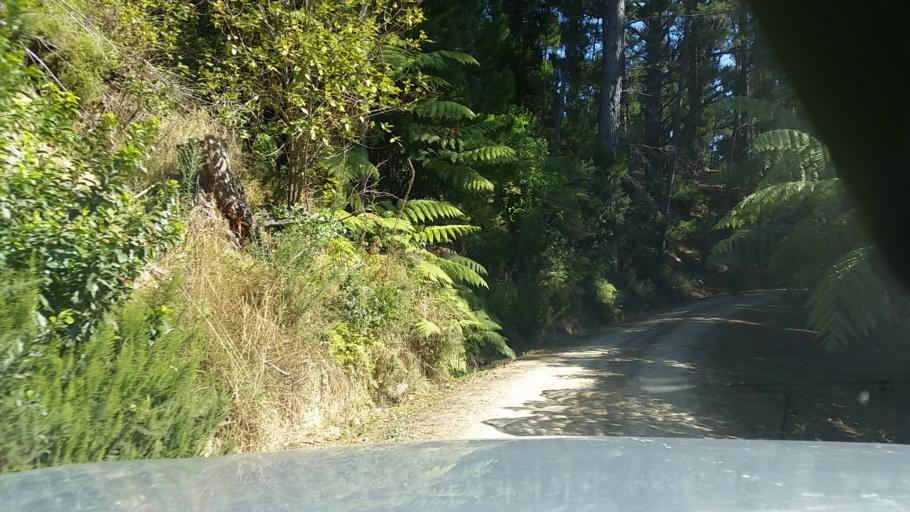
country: NZ
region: Marlborough
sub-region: Marlborough District
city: Picton
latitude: -41.2987
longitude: 174.1830
